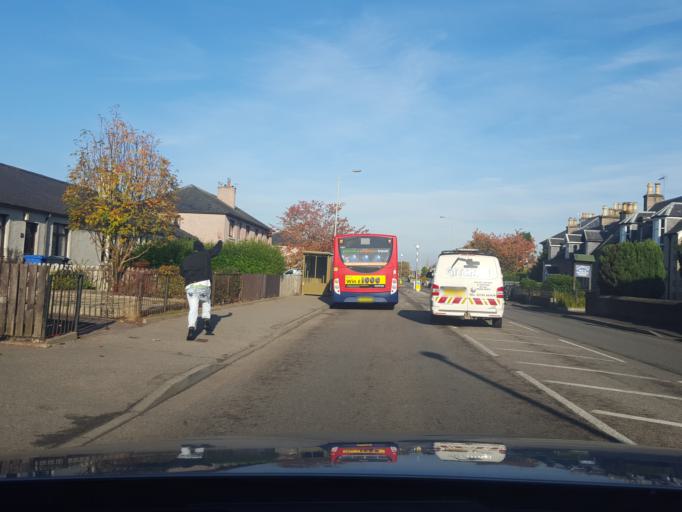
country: GB
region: Scotland
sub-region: Highland
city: Inverness
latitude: 57.4688
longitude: -4.2380
